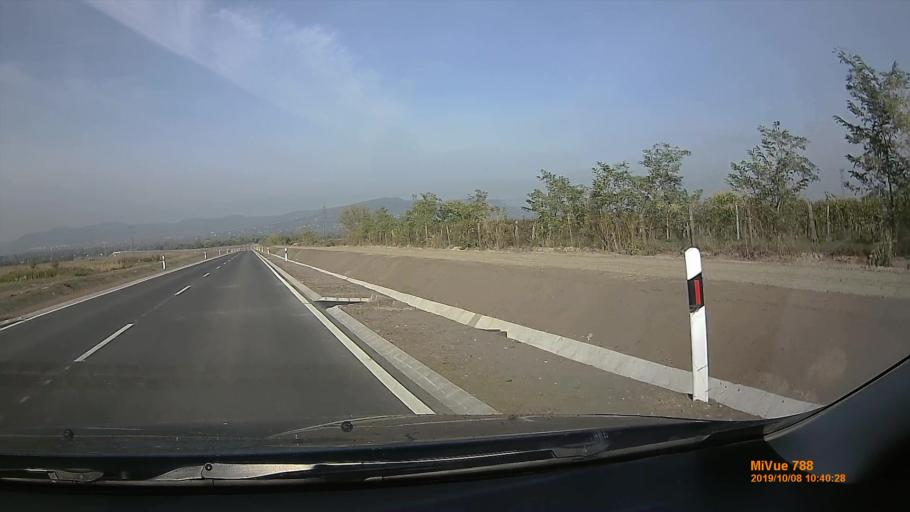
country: HU
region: Pest
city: God
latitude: 47.6618
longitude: 19.1450
